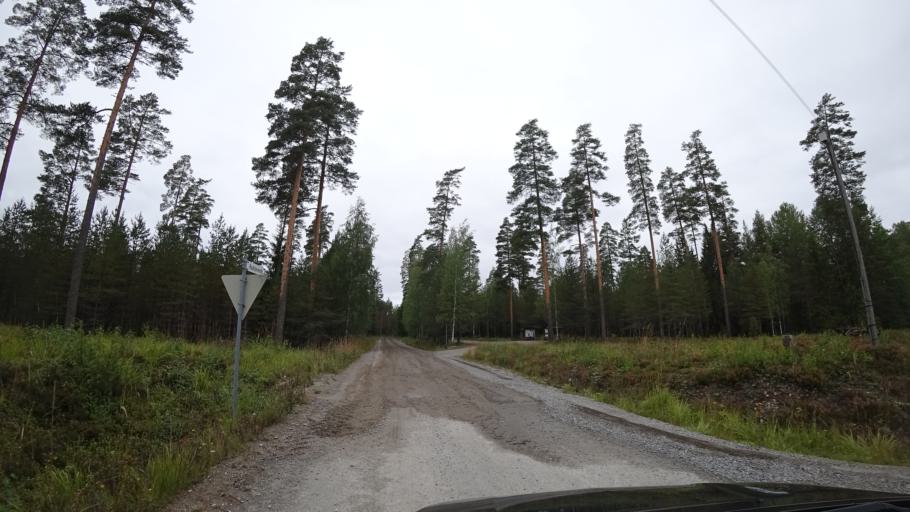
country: FI
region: Paijanne Tavastia
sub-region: Lahti
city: Auttoinen
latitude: 61.2118
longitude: 25.0874
